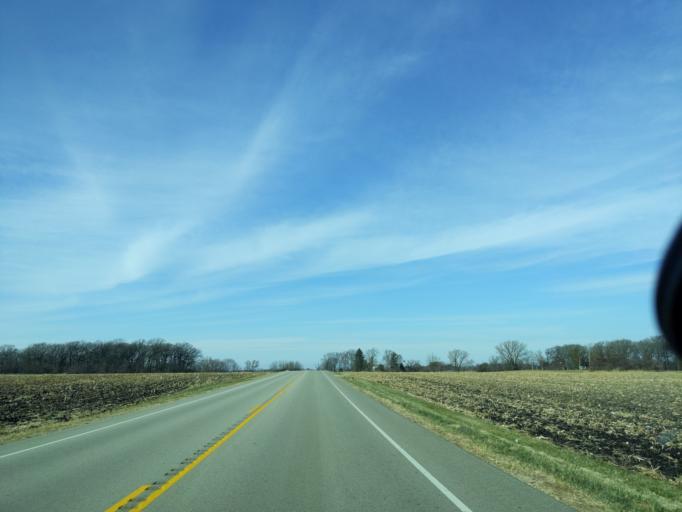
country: US
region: Wisconsin
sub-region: Walworth County
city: Elkhorn
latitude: 42.6948
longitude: -88.5649
